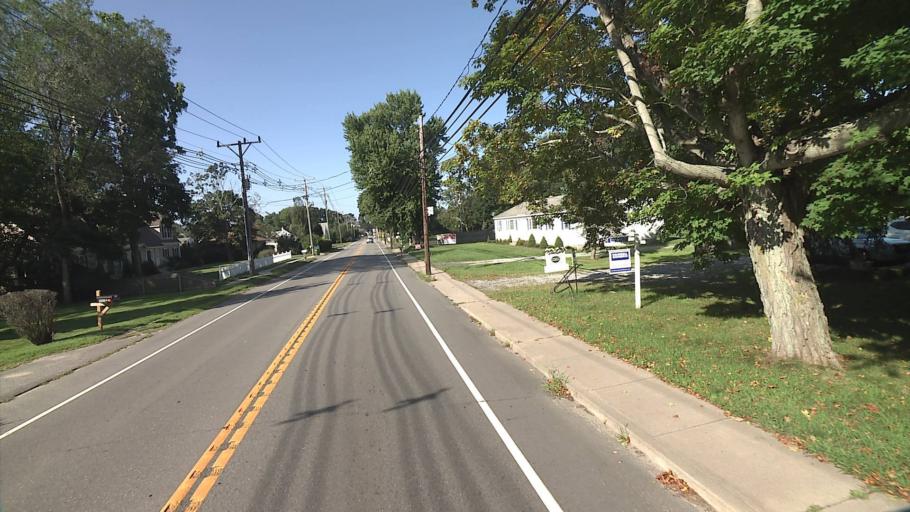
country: US
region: Connecticut
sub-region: Middlesex County
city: Westbrook Center
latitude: 41.2817
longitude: -72.4572
